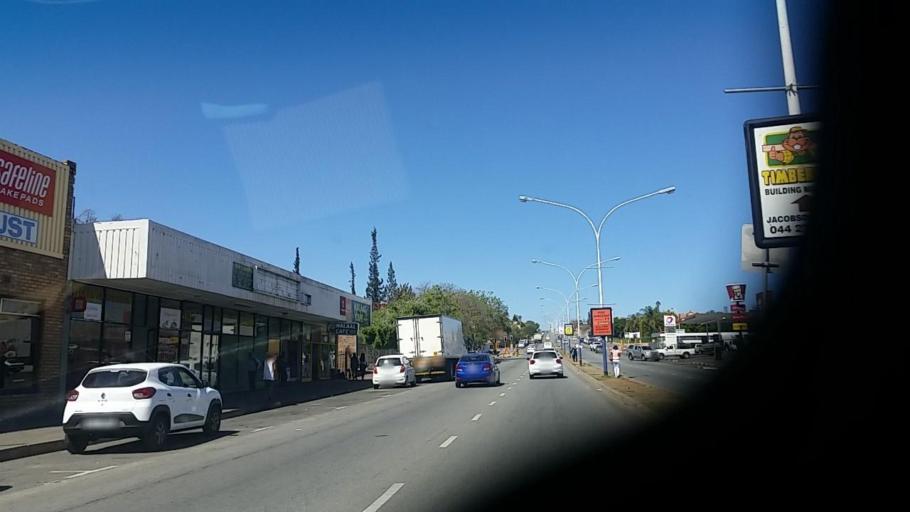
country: ZA
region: Western Cape
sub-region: Eden District Municipality
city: Oudtshoorn
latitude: -33.5931
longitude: 22.2051
